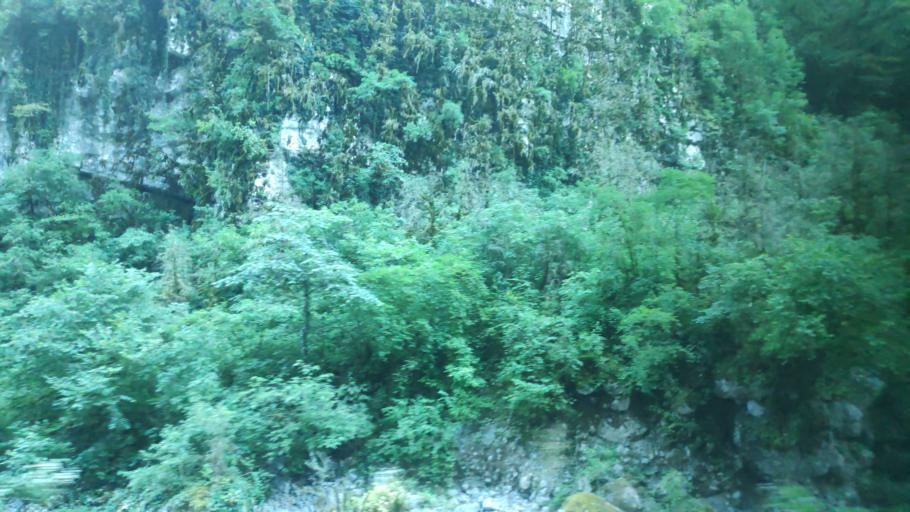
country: GE
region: Abkhazia
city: Gagra
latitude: 43.4376
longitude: 40.5331
